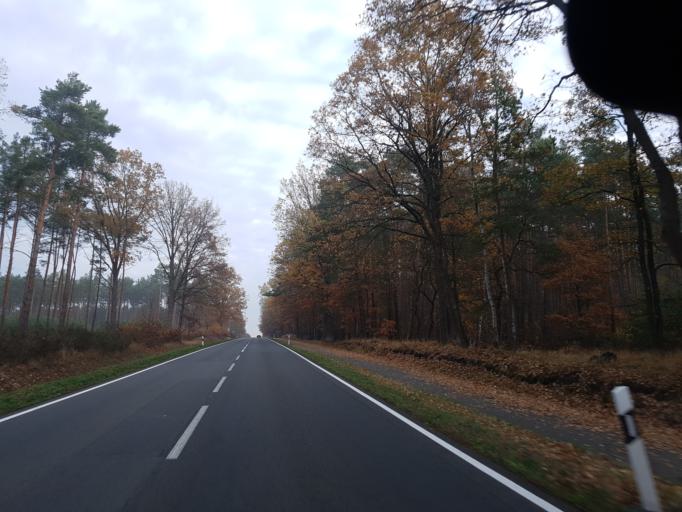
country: DE
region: Saxony-Anhalt
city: Kropstadt
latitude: 51.9845
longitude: 12.7645
